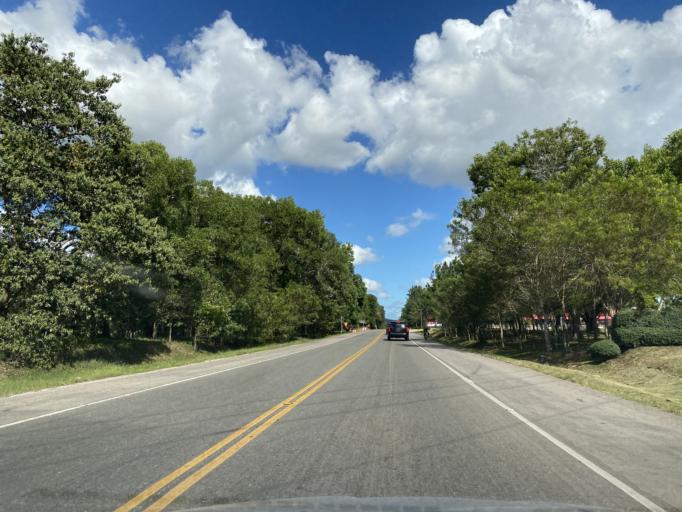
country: DO
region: Monte Plata
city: Monte Plata
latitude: 18.7681
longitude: -69.7553
